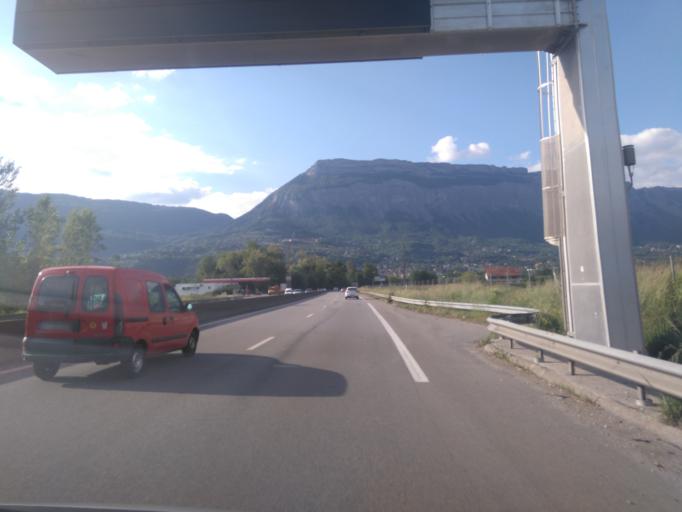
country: FR
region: Rhone-Alpes
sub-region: Departement de l'Isere
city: Gieres
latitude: 45.1960
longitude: 5.7818
